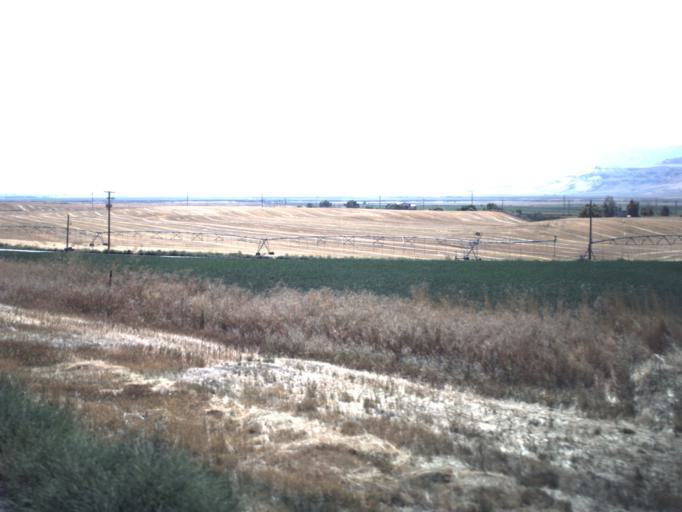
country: US
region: Utah
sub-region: Cache County
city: Benson
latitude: 41.8513
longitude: -111.9705
